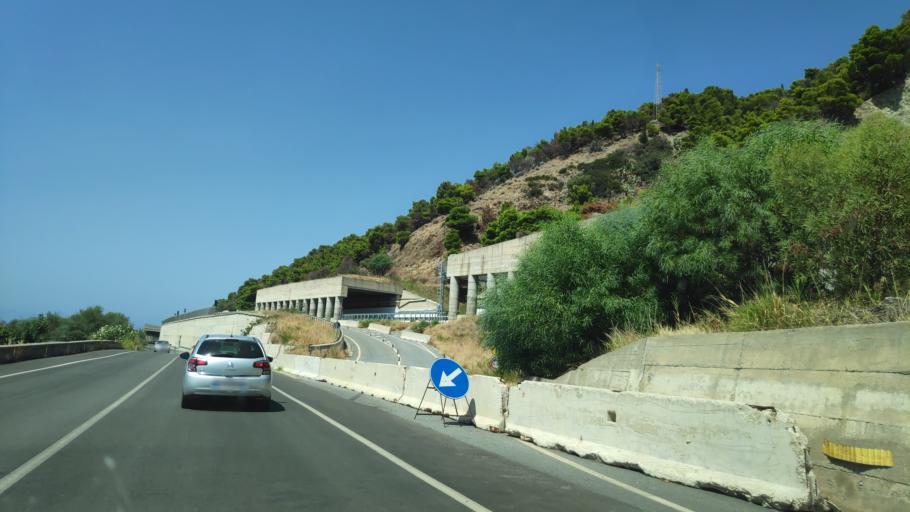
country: IT
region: Calabria
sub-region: Provincia di Reggio Calabria
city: Palizzi Marina
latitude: 37.9204
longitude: 15.9724
